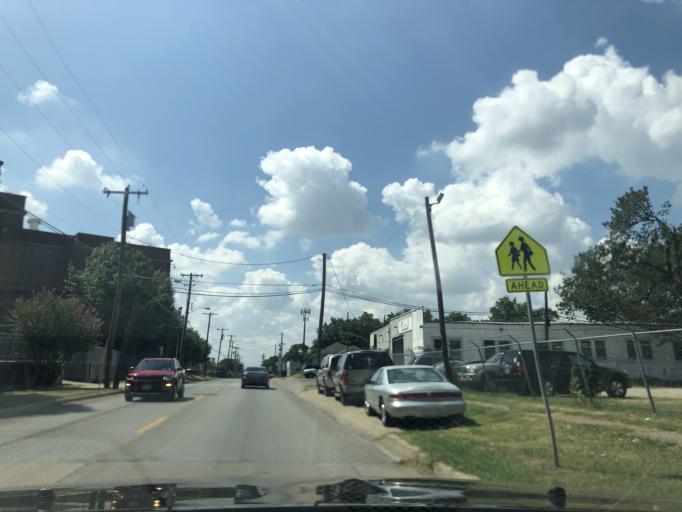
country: US
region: Texas
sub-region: Dallas County
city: Dallas
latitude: 32.7480
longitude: -96.8229
